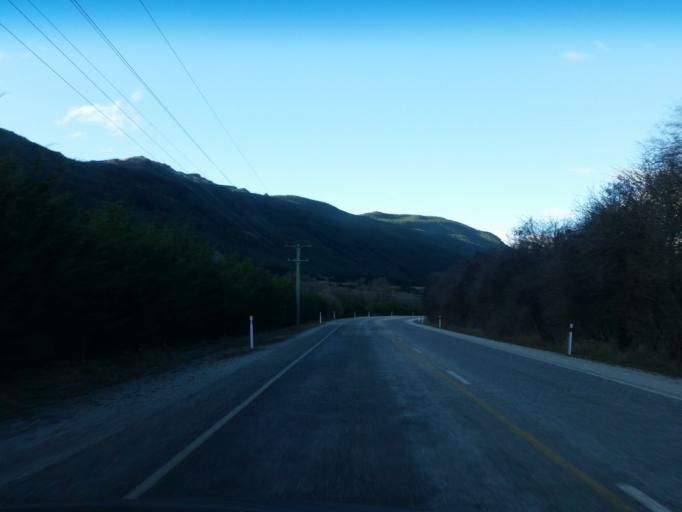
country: NZ
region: Otago
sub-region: Queenstown-Lakes District
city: Arrowtown
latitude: -44.9472
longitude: 168.7659
